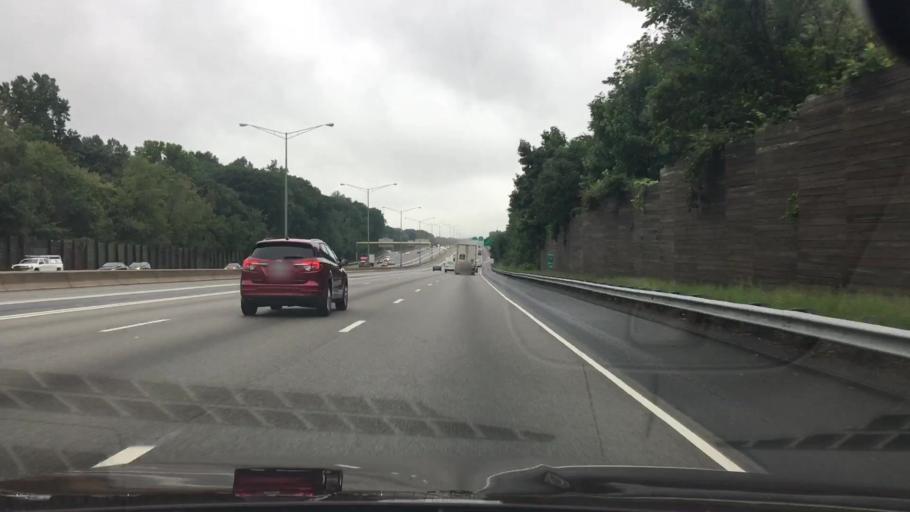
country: US
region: Connecticut
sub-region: Hartford County
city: Windsor
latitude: 41.8455
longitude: -72.6652
